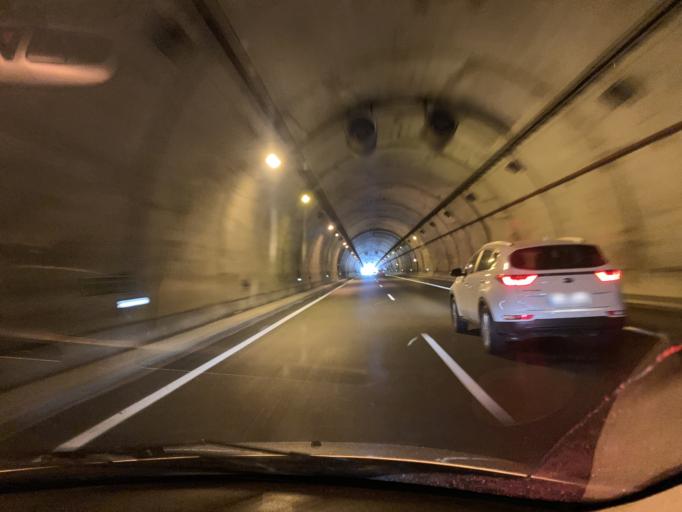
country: ES
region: Asturias
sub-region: Province of Asturias
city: Coana
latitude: 43.5372
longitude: -6.7523
